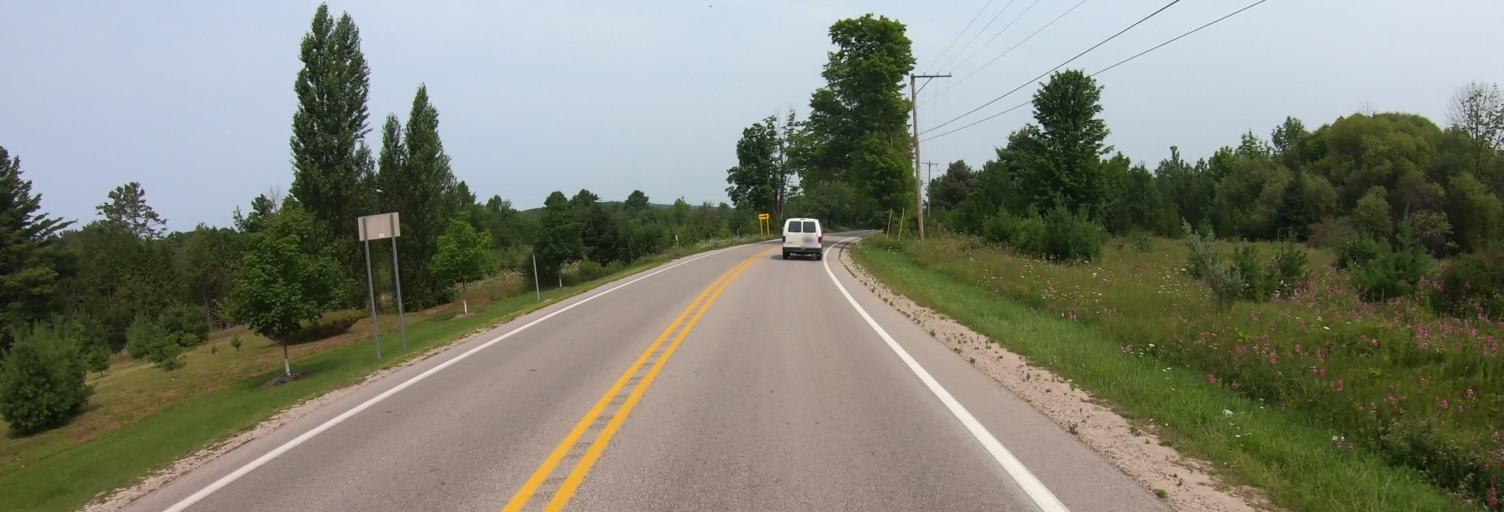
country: US
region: Michigan
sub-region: Leelanau County
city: Leland
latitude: 44.9855
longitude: -85.7738
